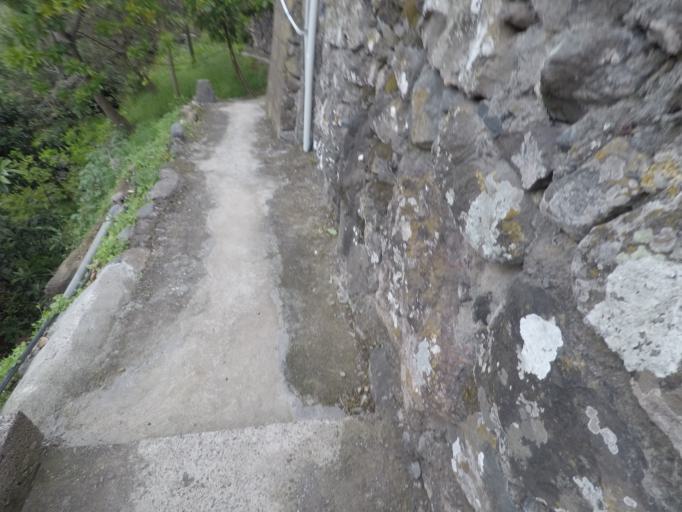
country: PT
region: Madeira
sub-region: Santana
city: Santana
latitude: 32.7807
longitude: -16.8471
